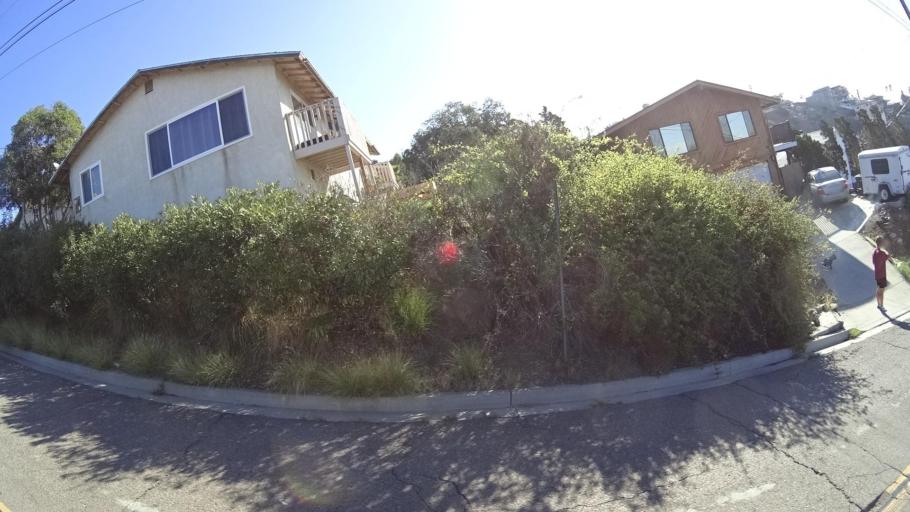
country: US
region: California
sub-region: San Diego County
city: La Presa
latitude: 32.7217
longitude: -116.9972
